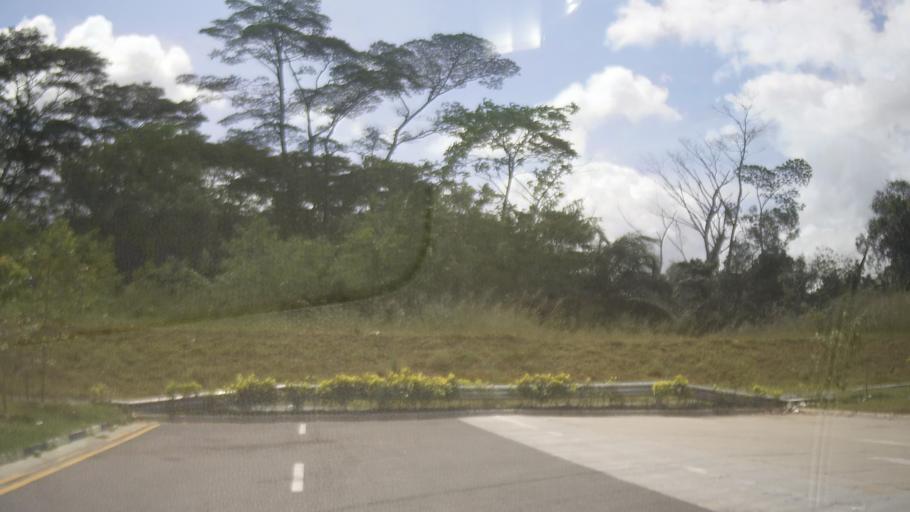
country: MY
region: Johor
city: Johor Bahru
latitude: 1.4283
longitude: 103.7536
